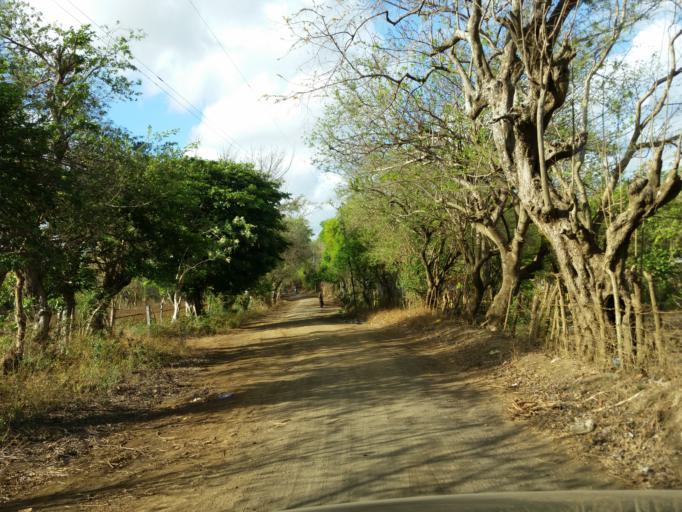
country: NI
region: Masaya
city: Nindiri
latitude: 12.0079
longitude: -86.0907
